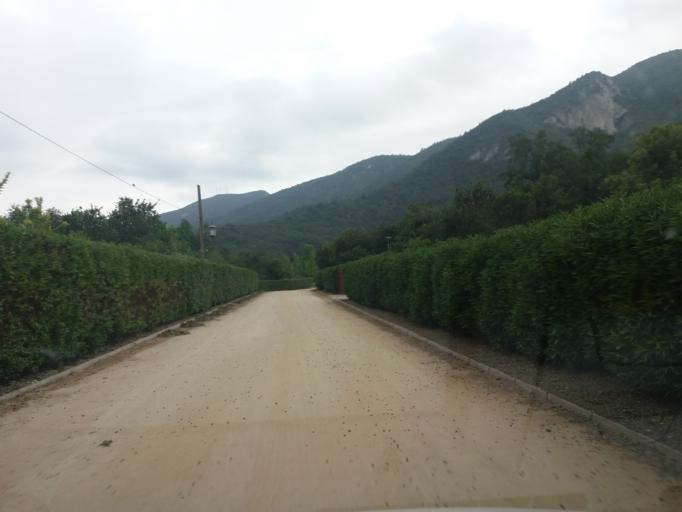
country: CL
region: Valparaiso
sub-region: Provincia de Marga Marga
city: Limache
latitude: -33.0269
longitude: -71.1365
